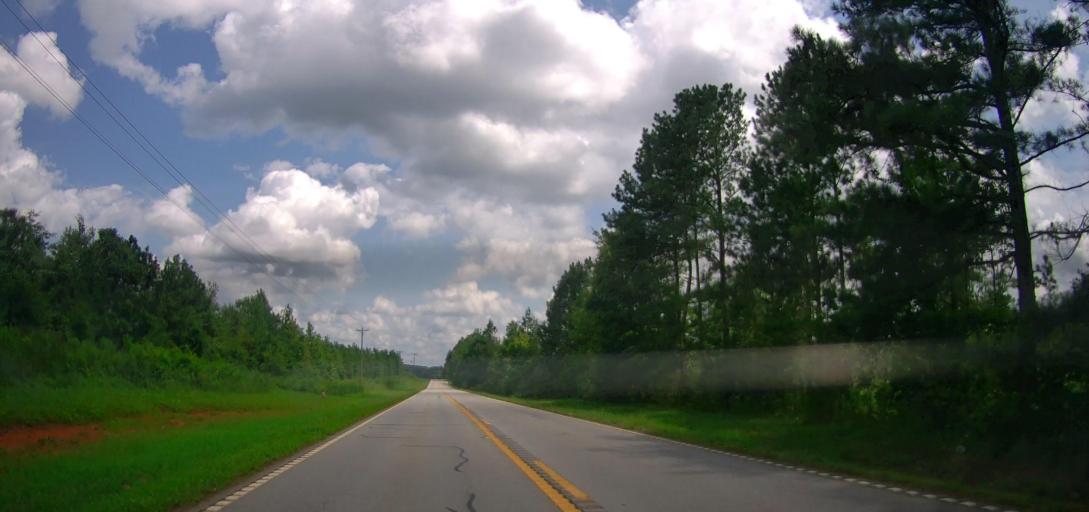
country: US
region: Georgia
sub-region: Heard County
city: Franklin
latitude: 33.3533
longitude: -85.1921
